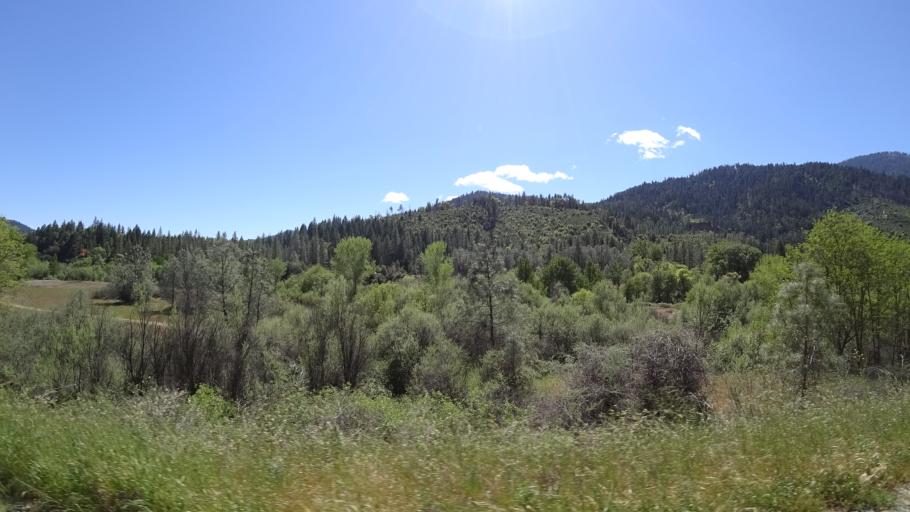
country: US
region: California
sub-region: Trinity County
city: Weaverville
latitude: 40.7256
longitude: -123.0521
